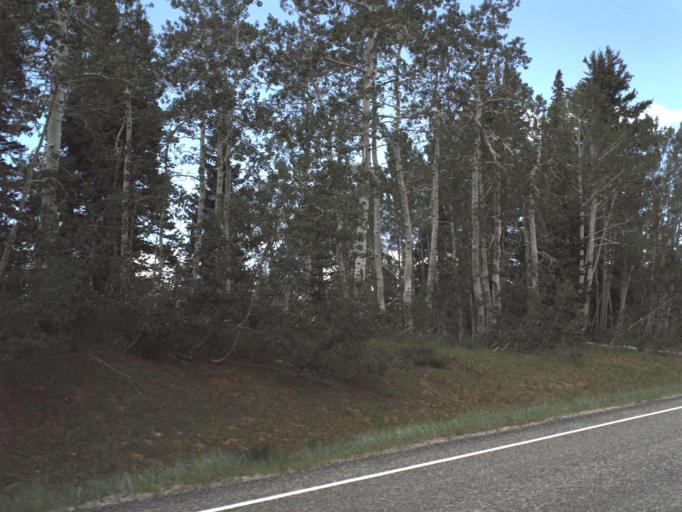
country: US
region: Utah
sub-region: Weber County
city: Wolf Creek
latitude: 41.4307
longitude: -111.5077
